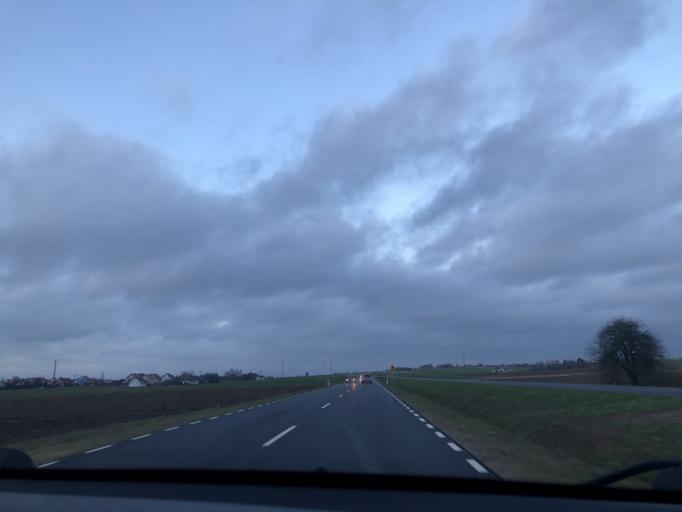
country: PL
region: Podlasie
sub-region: Lomza
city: Lomza
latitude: 53.1398
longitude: 22.0514
